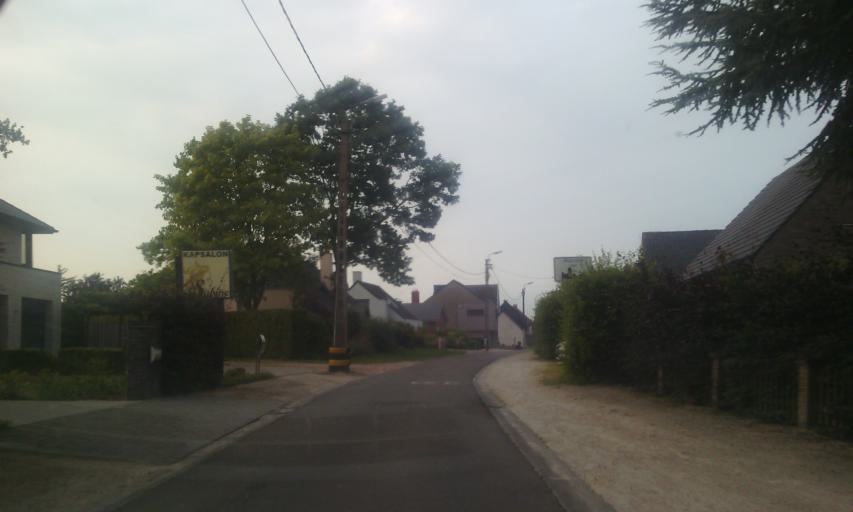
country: BE
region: Flanders
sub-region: Provincie Oost-Vlaanderen
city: Lede
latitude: 50.9684
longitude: 3.9544
